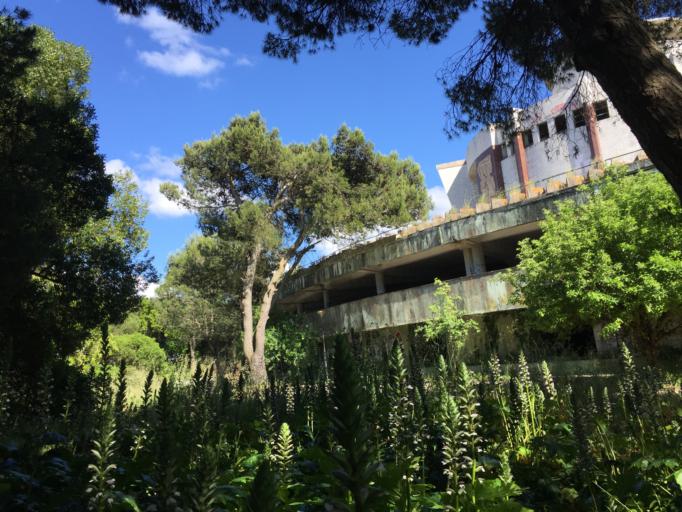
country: PT
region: Lisbon
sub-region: Odivelas
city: Pontinha
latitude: 38.7291
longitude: -9.1850
